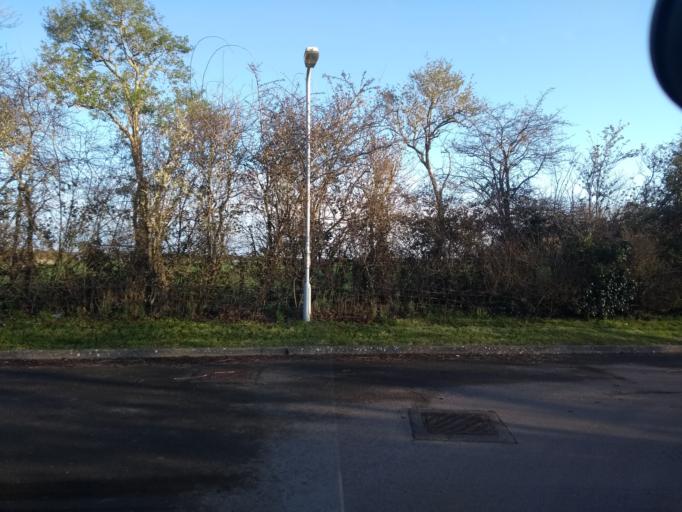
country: GB
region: England
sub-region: Somerset
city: Stoke-sub-Hamdon
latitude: 50.9563
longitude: -2.7532
